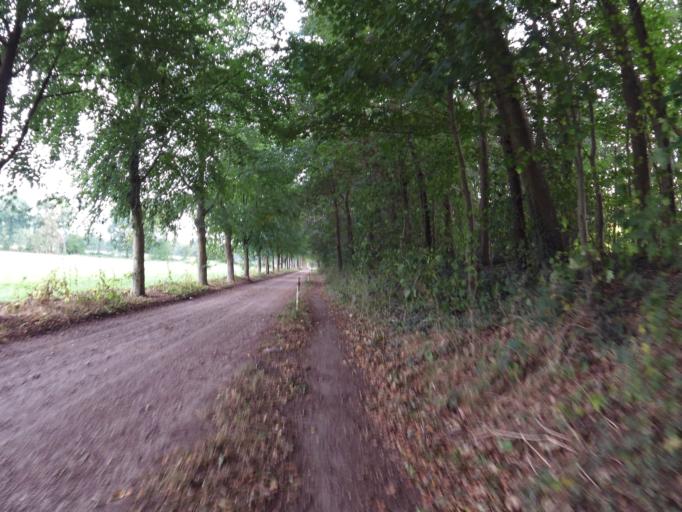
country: NL
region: North Brabant
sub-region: Gemeente Vught
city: Vught
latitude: 51.6649
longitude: 5.2429
